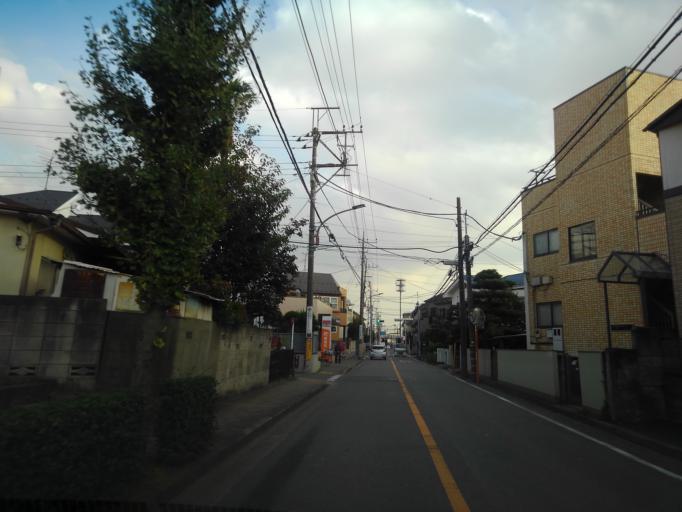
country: JP
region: Tokyo
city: Chofugaoka
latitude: 35.6657
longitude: 139.5406
